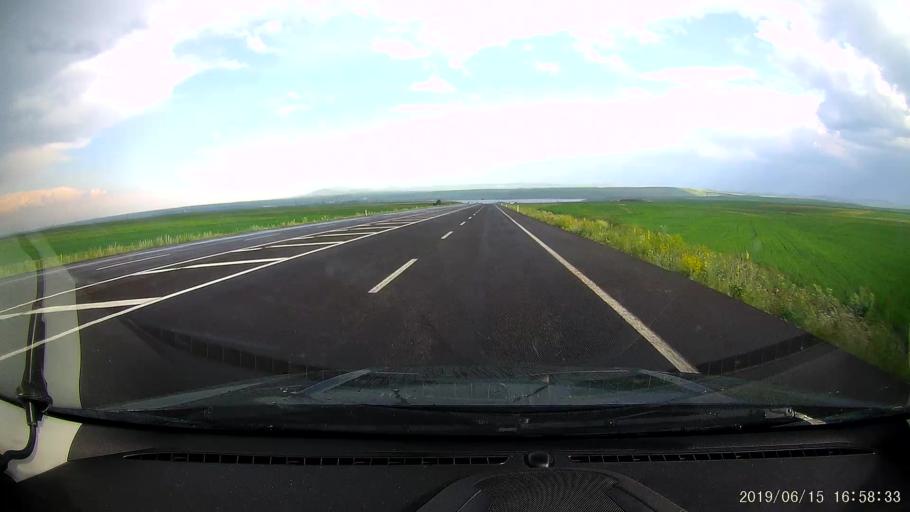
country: TR
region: Kars
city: Susuz
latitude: 40.7637
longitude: 43.1441
